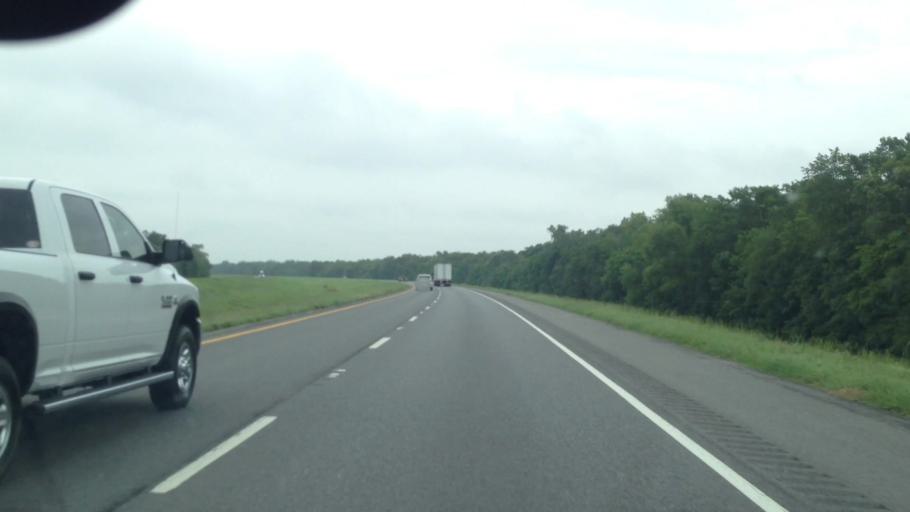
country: US
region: Louisiana
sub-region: Saint Landry Parish
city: Opelousas
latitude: 30.6894
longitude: -92.0792
